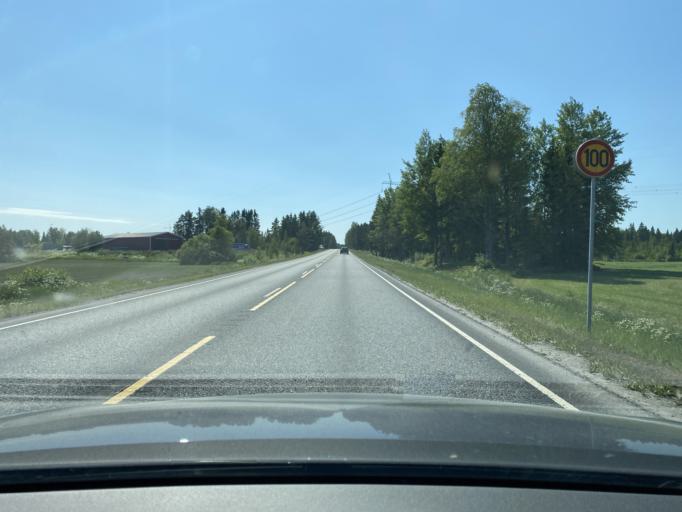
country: FI
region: Pirkanmaa
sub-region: Tampere
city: Nokia
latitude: 61.4163
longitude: 23.3187
